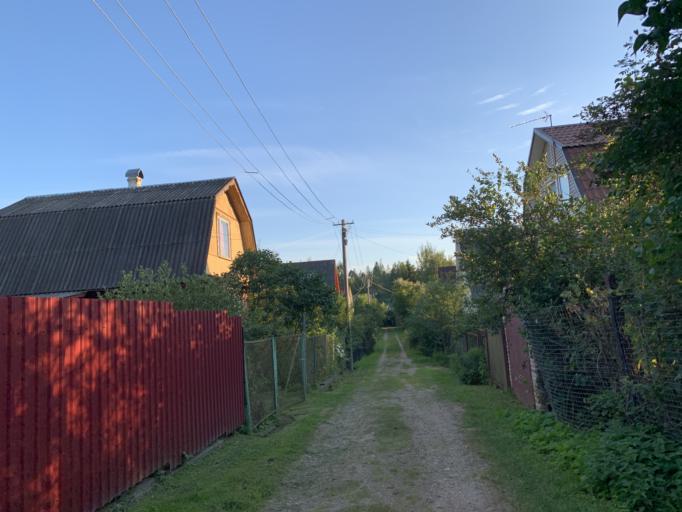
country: RU
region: Moskovskaya
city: Podosinki
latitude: 56.1787
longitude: 37.5795
